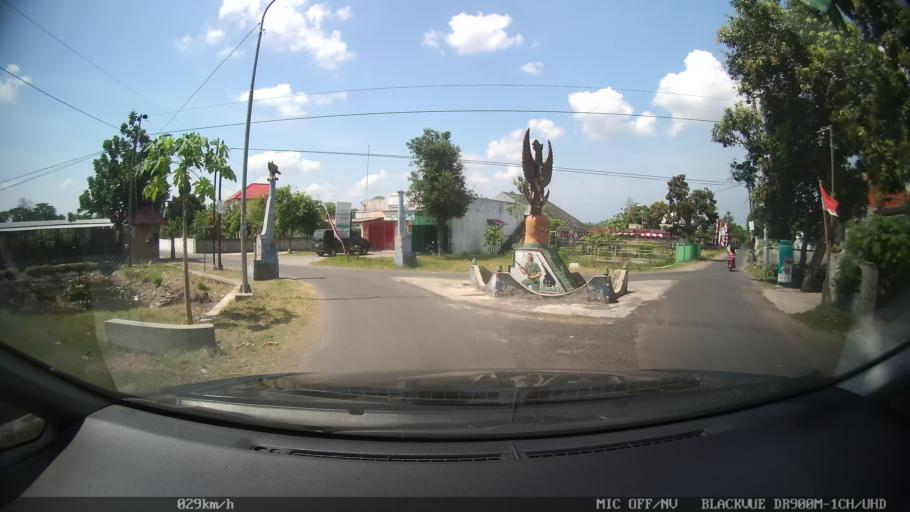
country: ID
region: Daerah Istimewa Yogyakarta
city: Sewon
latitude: -7.8473
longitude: 110.3854
